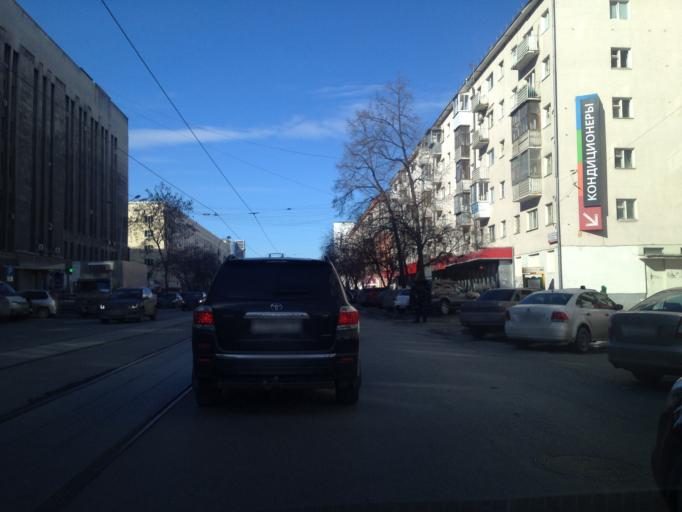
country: RU
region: Sverdlovsk
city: Yekaterinburg
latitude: 56.8371
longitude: 60.6216
